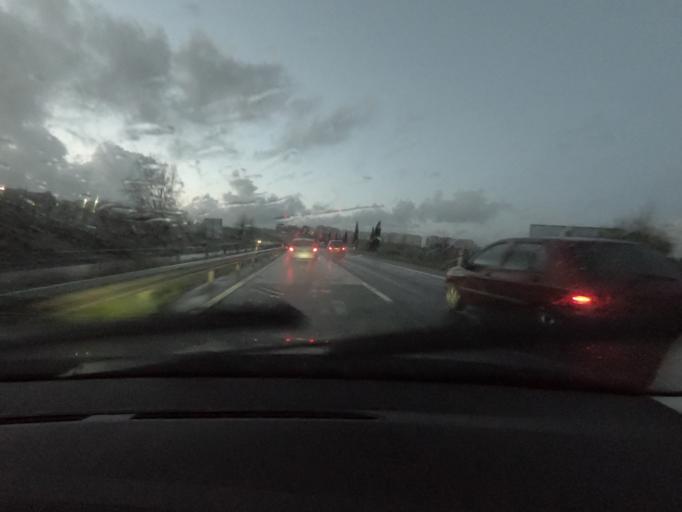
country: PT
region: Lisbon
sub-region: Oeiras
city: Barcarena
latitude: 38.7387
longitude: -9.2989
